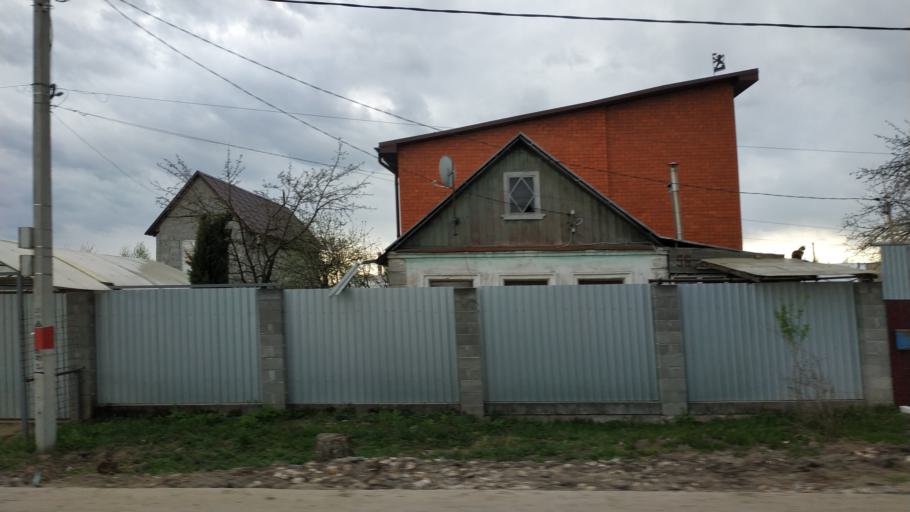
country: RU
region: Moskovskaya
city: Pavlovskiy Posad
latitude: 55.7686
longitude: 38.6952
